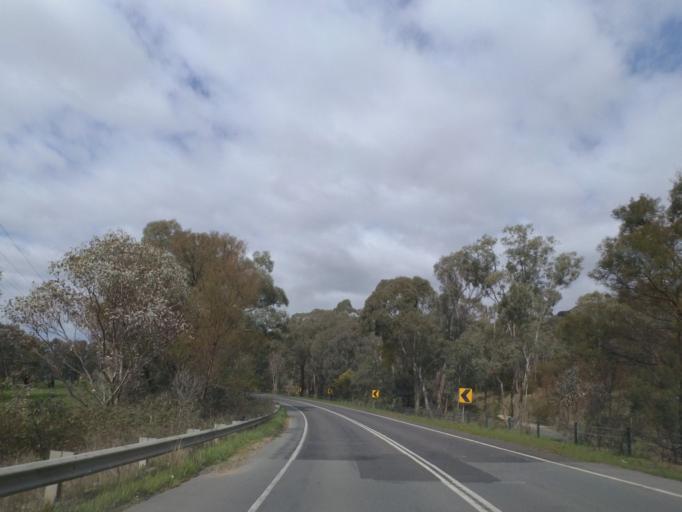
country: AU
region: Victoria
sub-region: Murrindindi
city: Kinglake West
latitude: -37.1259
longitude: 145.2216
